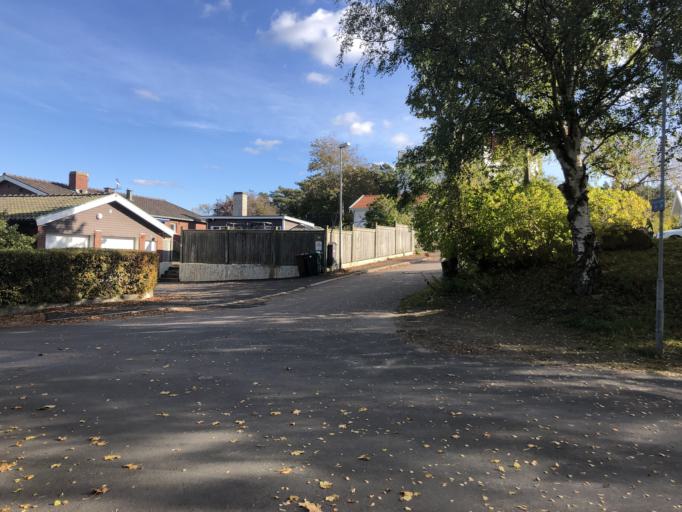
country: SE
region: Vaestra Goetaland
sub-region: Goteborg
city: Majorna
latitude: 57.6341
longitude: 11.9242
